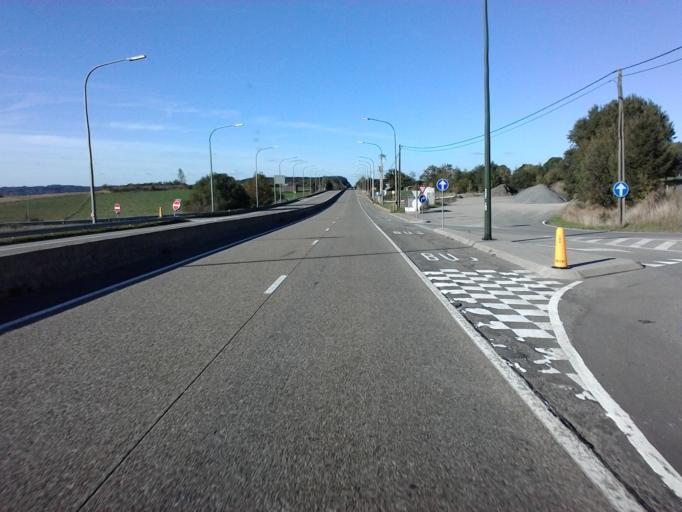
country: BE
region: Wallonia
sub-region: Province du Luxembourg
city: Bastogne
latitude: 49.9242
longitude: 5.7048
